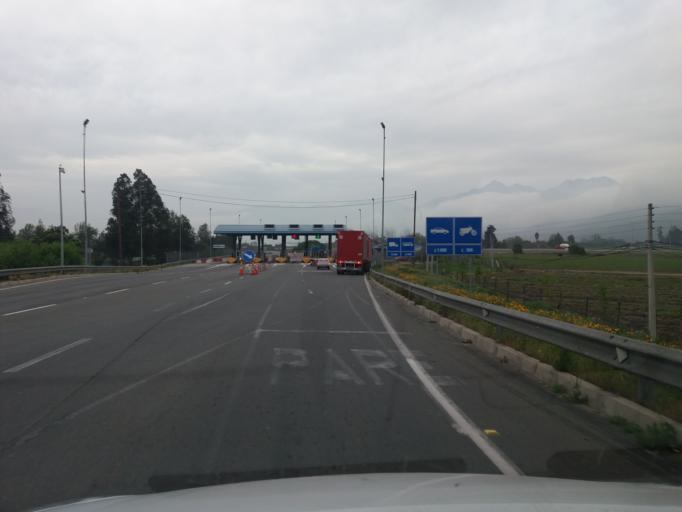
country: CL
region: Valparaiso
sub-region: Provincia de Quillota
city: Quillota
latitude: -32.9278
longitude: -71.2877
